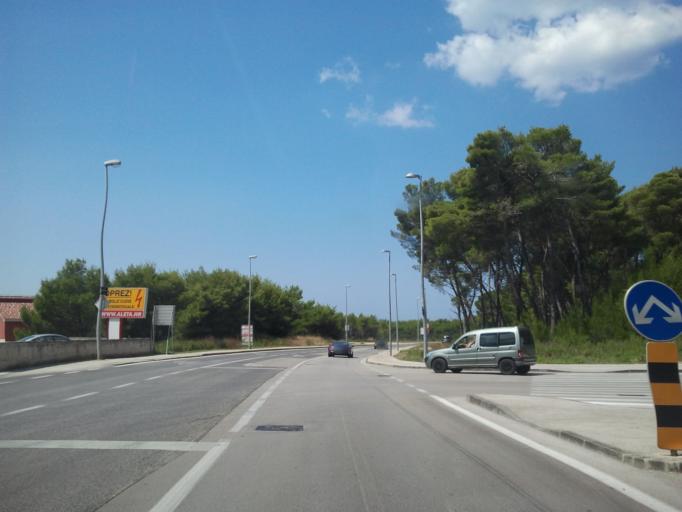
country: HR
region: Zadarska
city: Zadar
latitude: 44.1389
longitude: 15.2380
